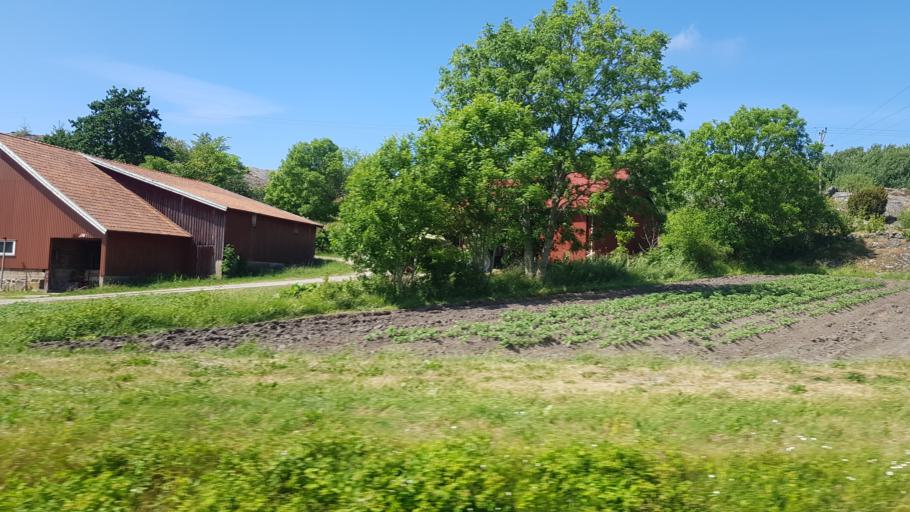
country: SE
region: Vaestra Goetaland
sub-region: Tjorns Kommun
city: Skaerhamn
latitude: 57.9774
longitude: 11.5633
